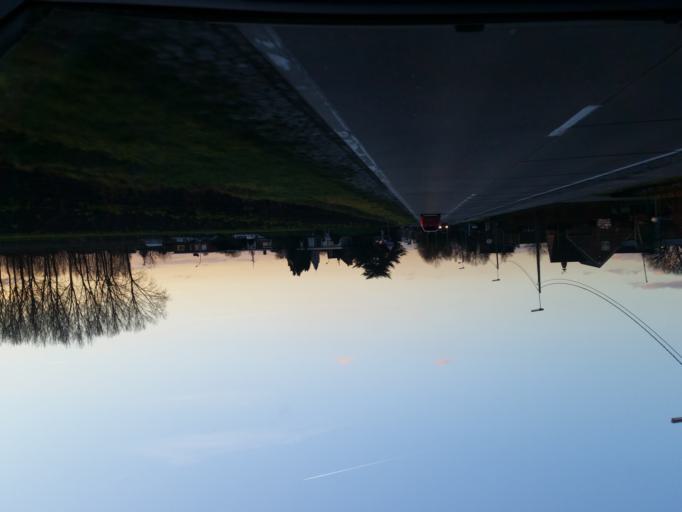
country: BE
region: Flanders
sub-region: Provincie Oost-Vlaanderen
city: Sint-Gillis-Waas
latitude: 51.2631
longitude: 4.1875
